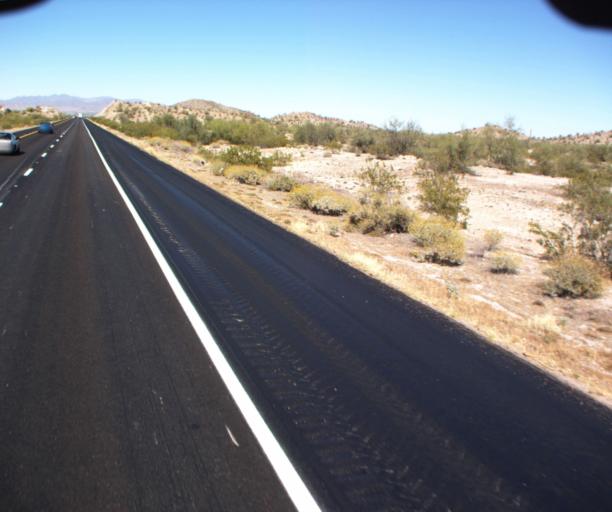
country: US
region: Arizona
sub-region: Maricopa County
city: Buckeye
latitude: 33.2938
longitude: -112.6281
